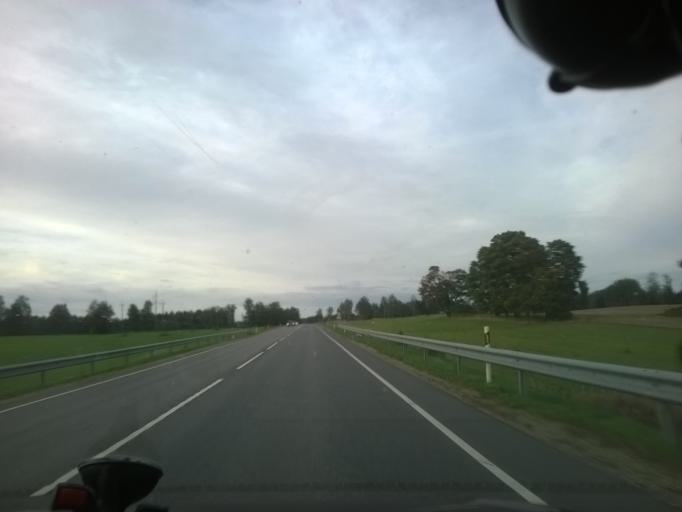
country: EE
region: Vorumaa
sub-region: Antsla vald
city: Vana-Antsla
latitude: 57.9924
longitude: 26.7653
